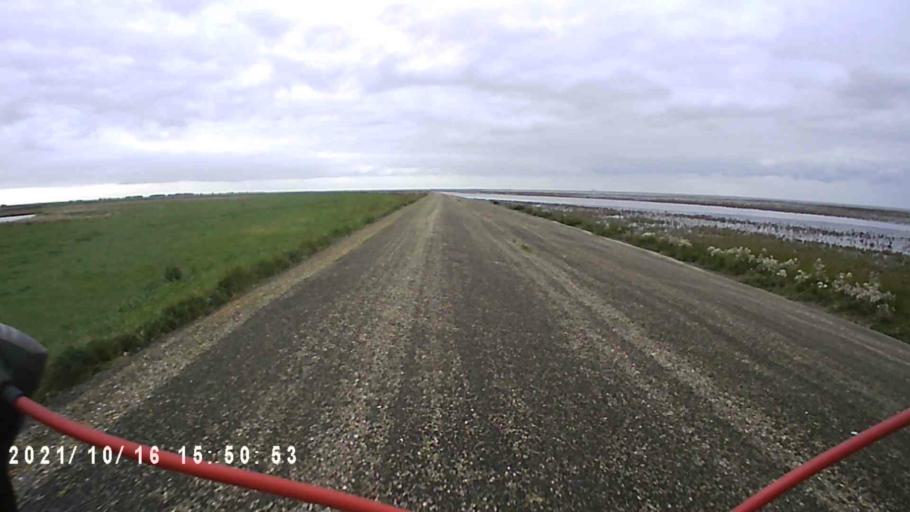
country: NL
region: Friesland
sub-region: Gemeente Dongeradeel
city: Anjum
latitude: 53.4041
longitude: 6.1353
